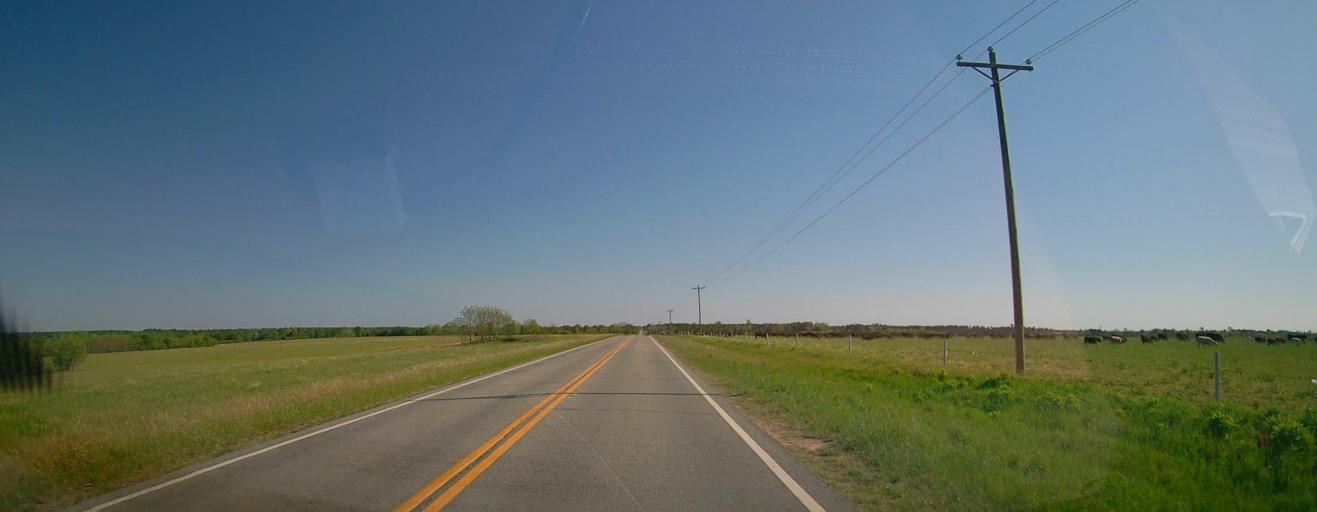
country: US
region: Georgia
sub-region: Wilcox County
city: Rochelle
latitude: 31.8856
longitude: -83.4888
